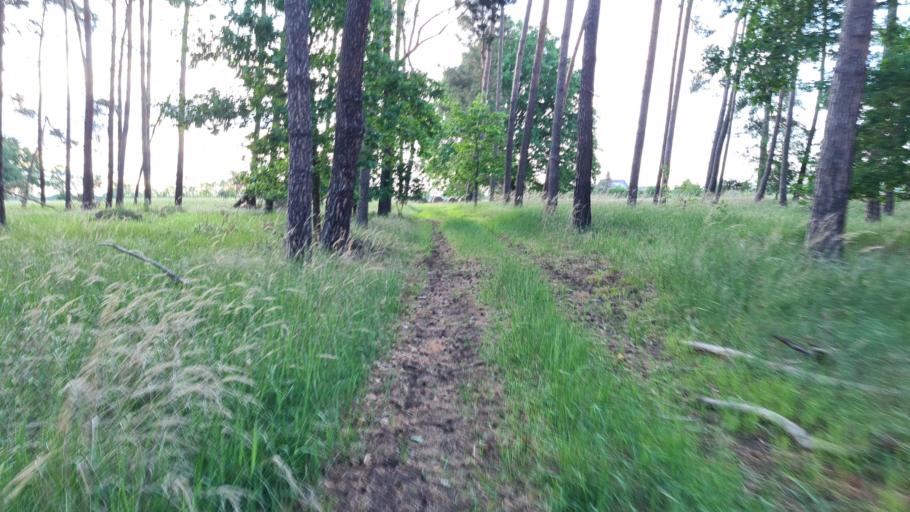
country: DE
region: Brandenburg
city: Schilda
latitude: 51.6082
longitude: 13.3547
